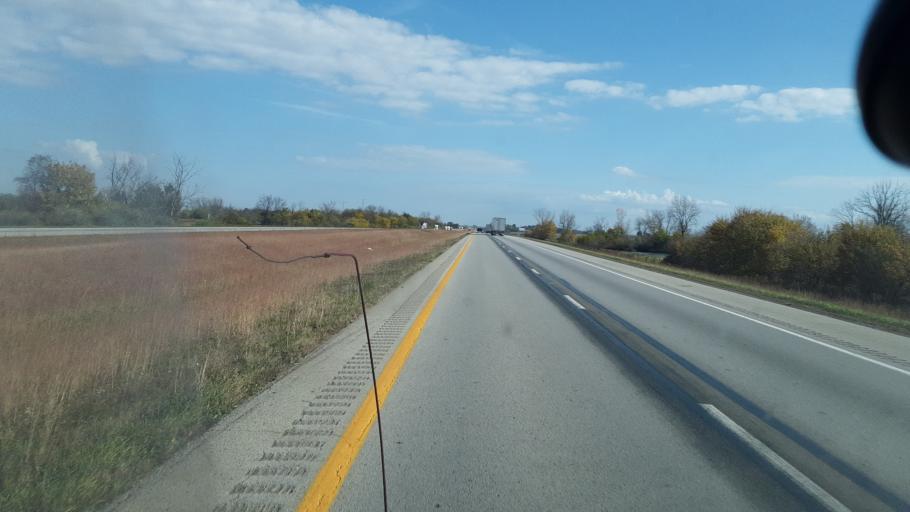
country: US
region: Ohio
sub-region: Greene County
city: Jamestown
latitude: 39.5698
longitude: -83.7003
